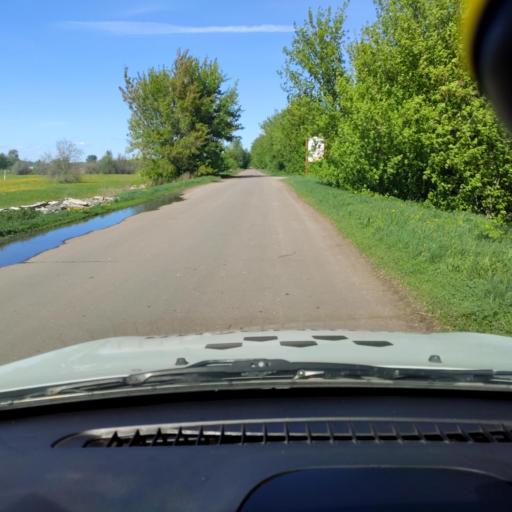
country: RU
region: Samara
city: Tol'yatti
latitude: 53.6675
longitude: 49.4363
